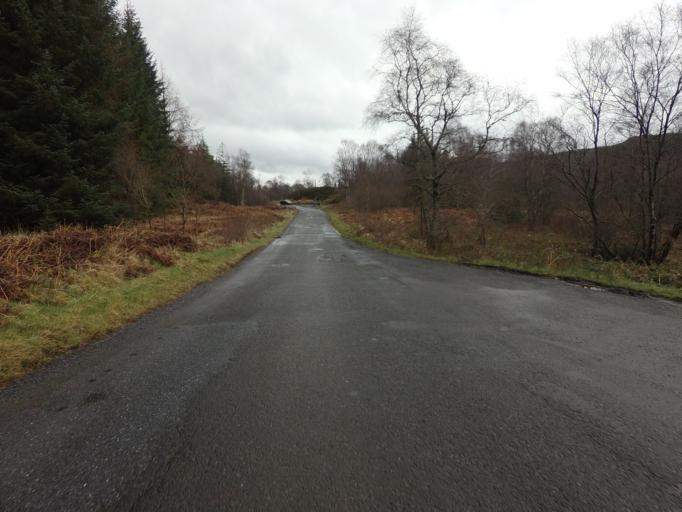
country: GB
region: Scotland
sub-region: West Dunbartonshire
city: Balloch
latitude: 56.2006
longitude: -4.5278
